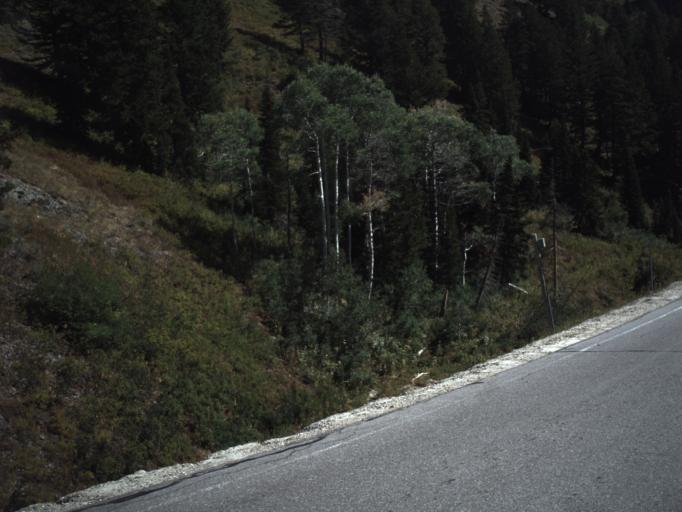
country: US
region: Utah
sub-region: Weber County
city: Wolf Creek
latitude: 41.3740
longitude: -111.7826
